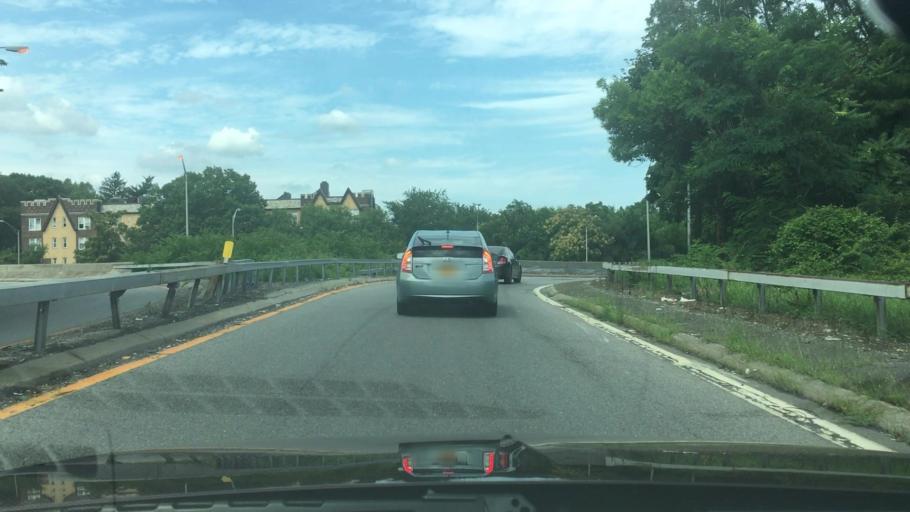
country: US
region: New York
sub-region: Westchester County
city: Bronxville
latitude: 40.9275
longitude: -73.8416
